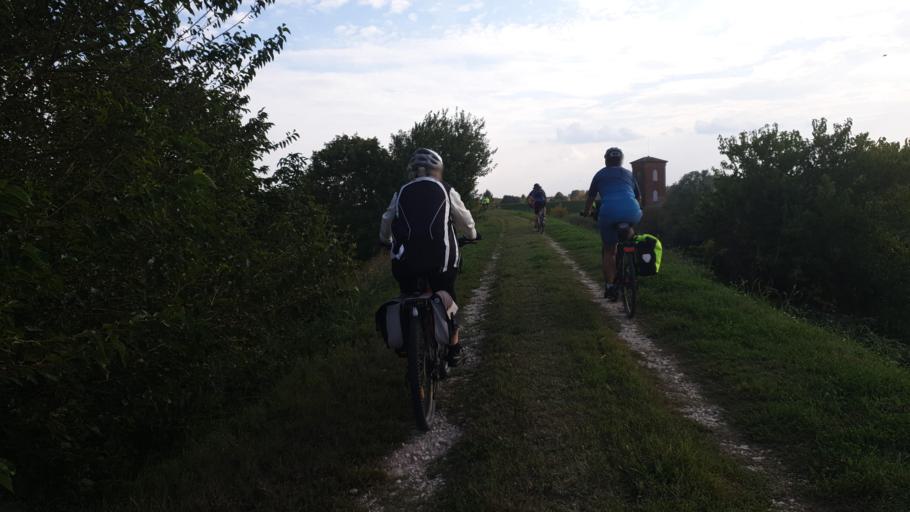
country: IT
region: Veneto
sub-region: Provincia di Padova
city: Montagnana
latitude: 45.2566
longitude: 11.4770
